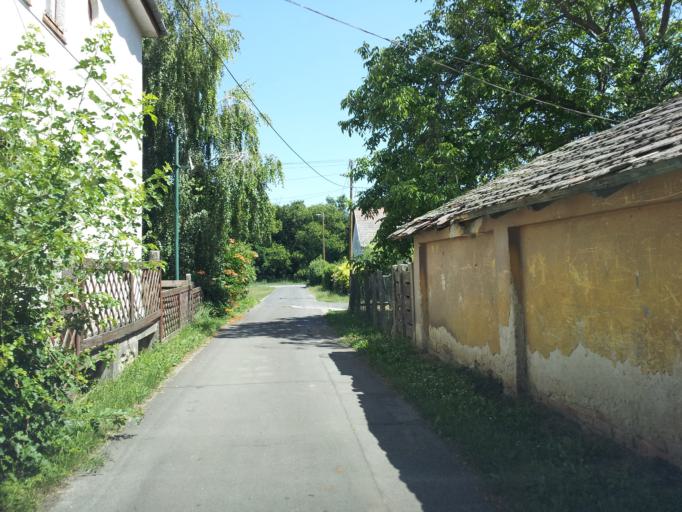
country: HU
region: Veszprem
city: Berhida
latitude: 47.1146
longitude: 18.1047
